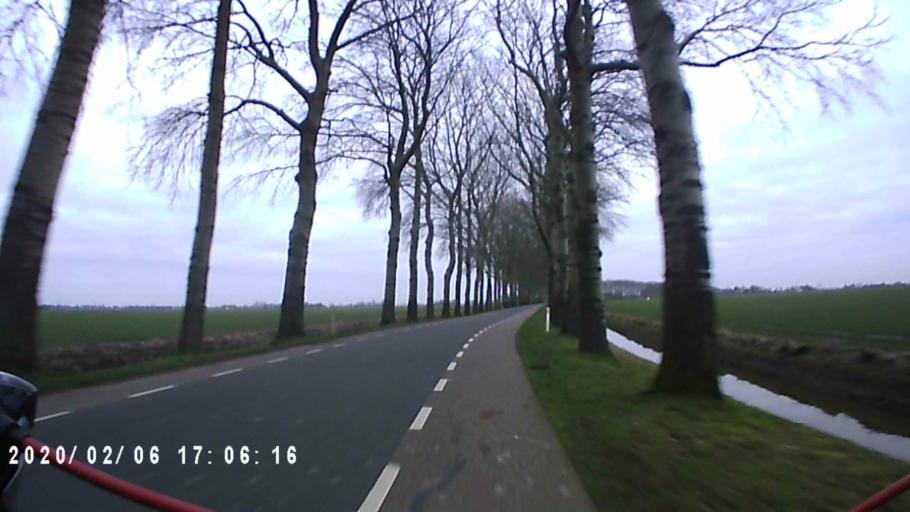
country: NL
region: Groningen
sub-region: Gemeente Winsum
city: Winsum
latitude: 53.2748
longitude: 6.5132
